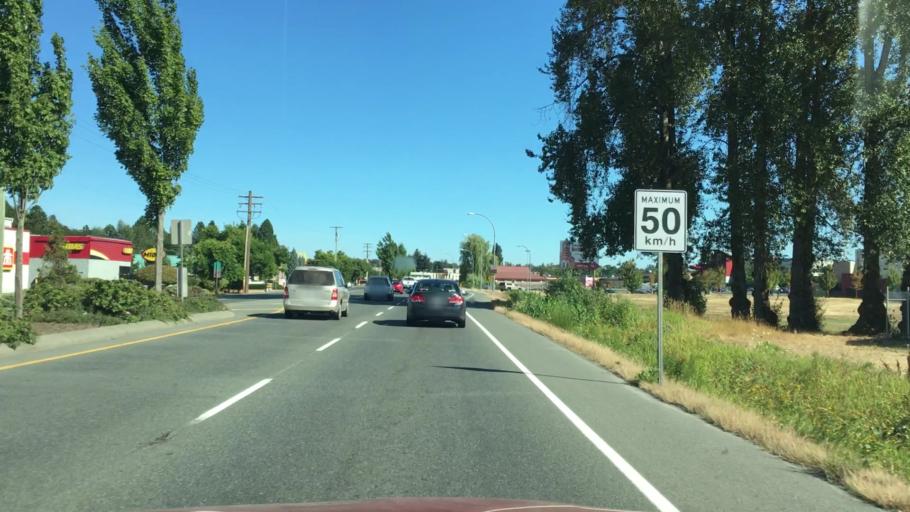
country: CA
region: British Columbia
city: Duncan
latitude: 48.7853
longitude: -123.7040
